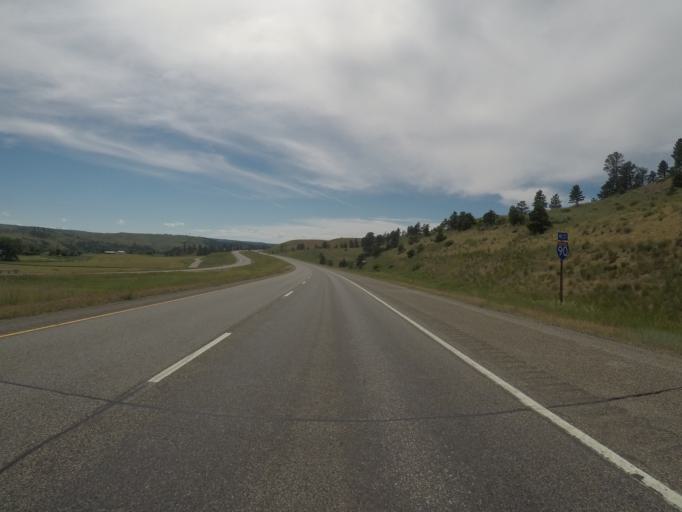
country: US
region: Montana
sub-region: Stillwater County
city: Columbus
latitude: 45.5987
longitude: -109.0735
